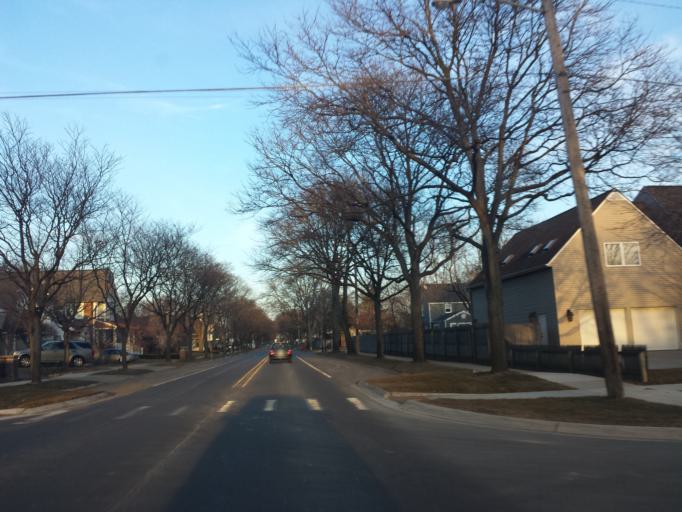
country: US
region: Michigan
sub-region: Oakland County
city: Birmingham
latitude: 42.5387
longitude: -83.2207
